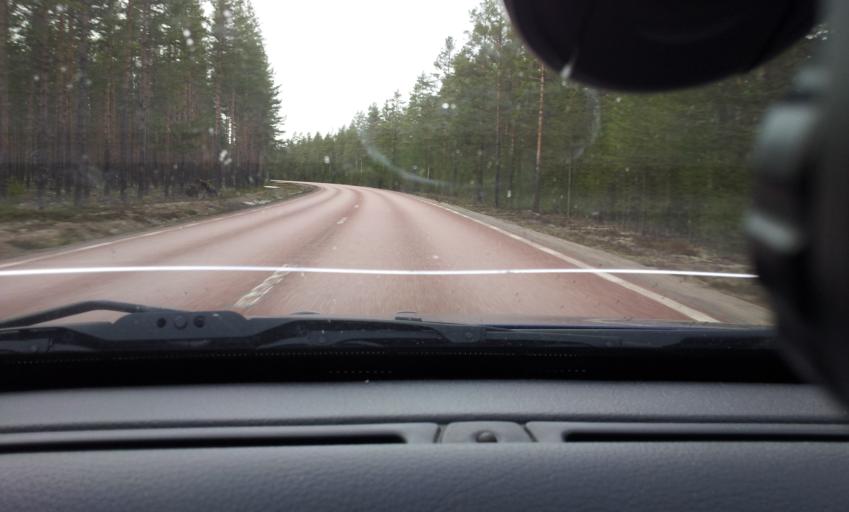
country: SE
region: Gaevleborg
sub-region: Ljusdals Kommun
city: Farila
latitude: 61.9131
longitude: 15.6259
